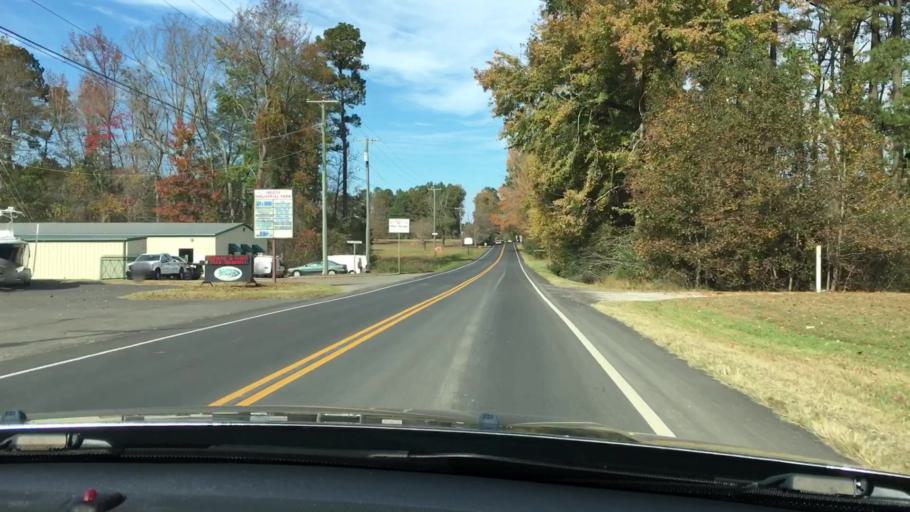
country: US
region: Virginia
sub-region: King William County
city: West Point
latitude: 37.4563
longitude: -76.8410
